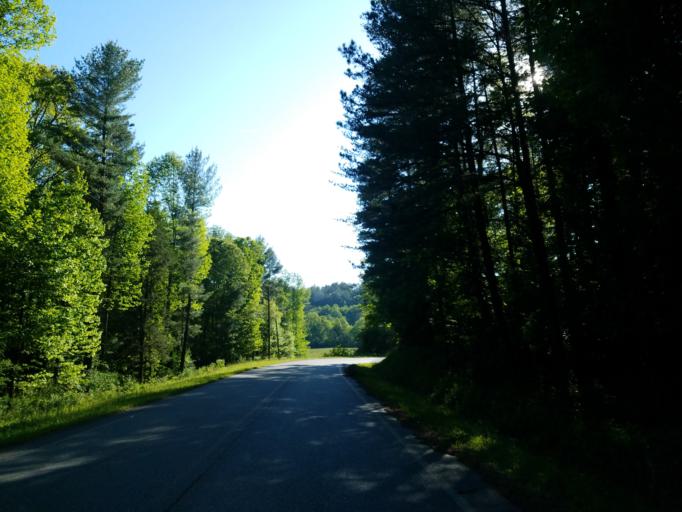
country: US
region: Georgia
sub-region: Fannin County
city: Blue Ridge
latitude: 34.7447
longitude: -84.1475
